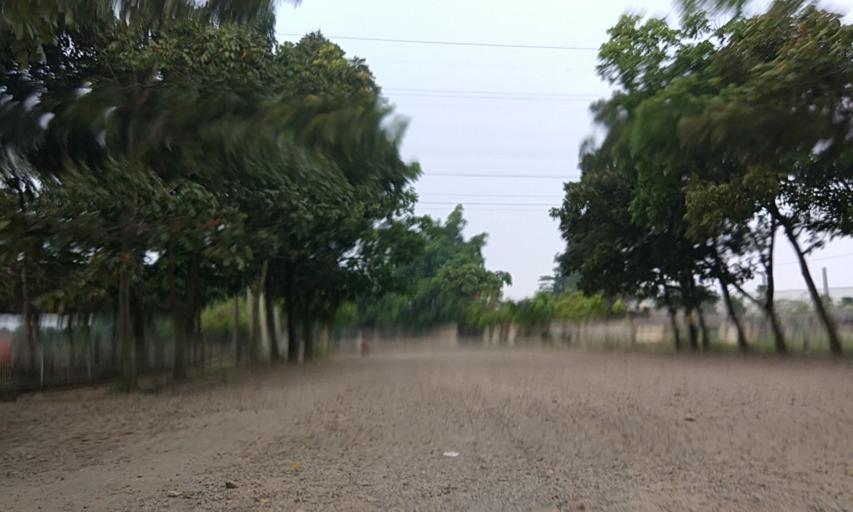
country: ID
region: West Java
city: Bandung
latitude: -6.9090
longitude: 107.6702
